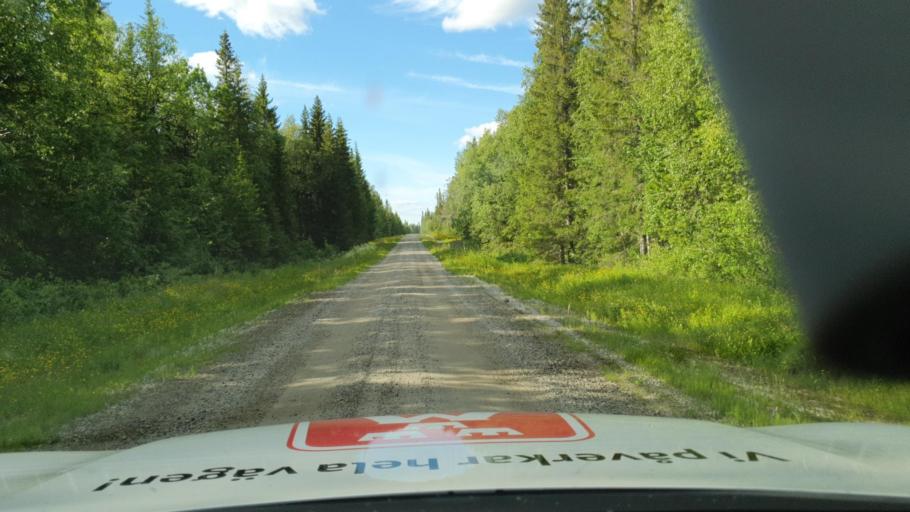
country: SE
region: Vaesterbotten
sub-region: Lycksele Kommun
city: Lycksele
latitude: 64.4339
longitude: 18.2727
